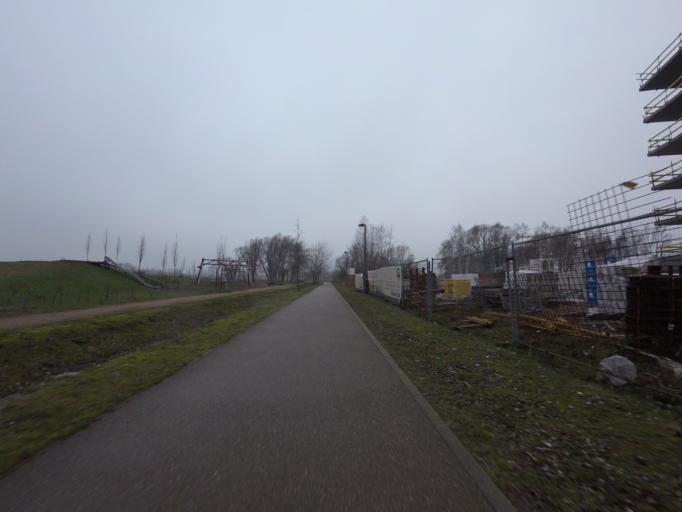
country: BE
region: Flanders
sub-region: Provincie Antwerpen
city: Antwerpen
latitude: 51.2165
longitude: 4.3702
